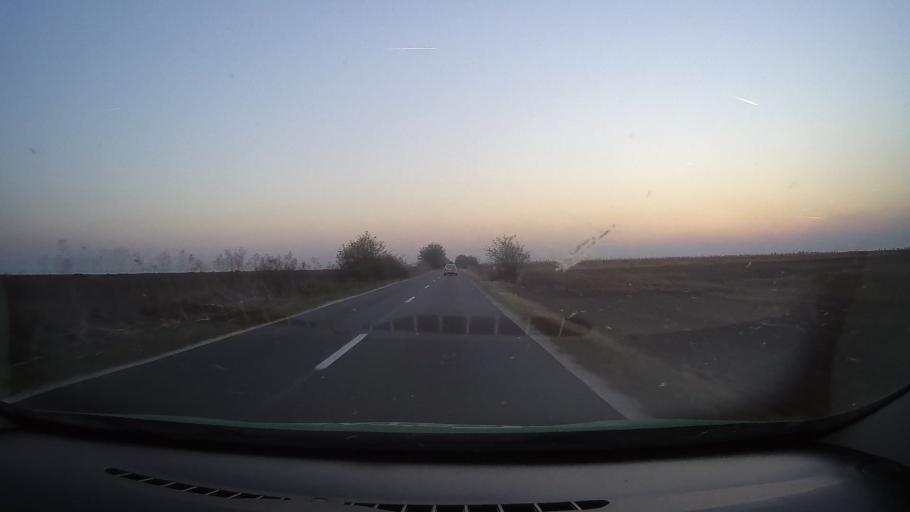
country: RO
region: Arad
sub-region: Comuna Zimandu Nou
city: Zimandu Nou
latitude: 46.3017
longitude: 21.4308
